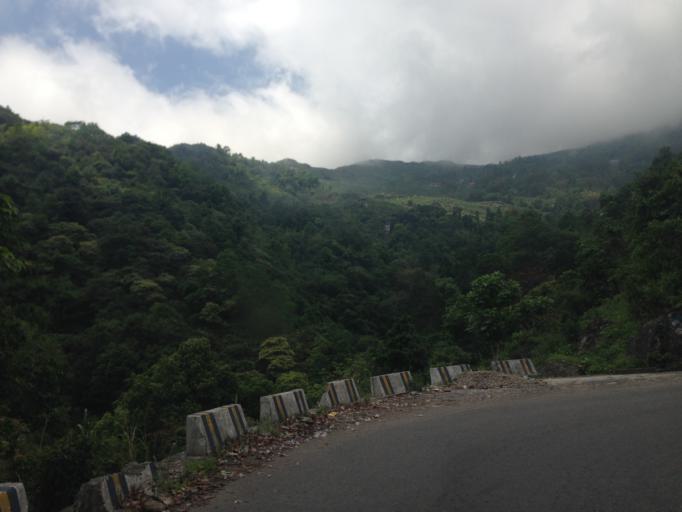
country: IN
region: West Bengal
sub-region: Darjiling
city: Karsiyang
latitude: 26.8576
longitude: 88.2941
